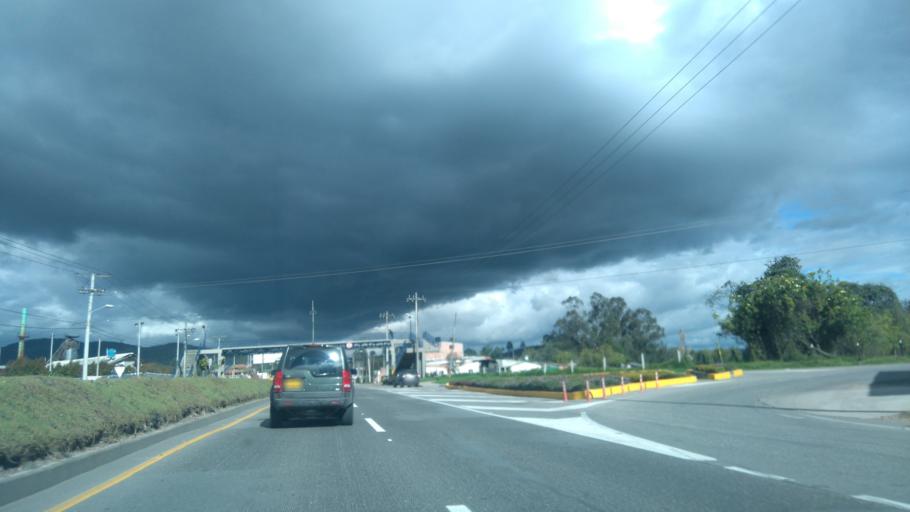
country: CO
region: Cundinamarca
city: El Rosal
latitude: 4.8197
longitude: -74.2296
